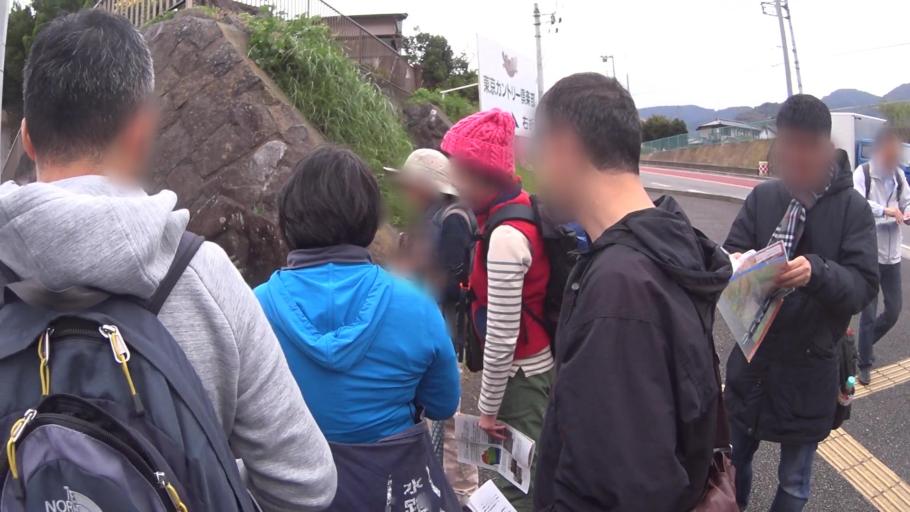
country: JP
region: Kanagawa
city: Hadano
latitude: 35.3934
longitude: 139.2345
